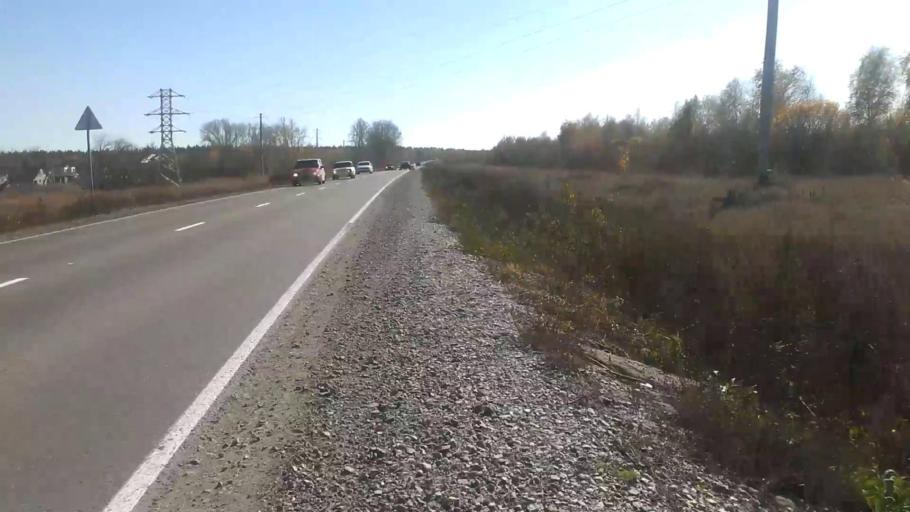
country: RU
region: Altai Krai
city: Sannikovo
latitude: 53.3109
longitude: 83.9661
